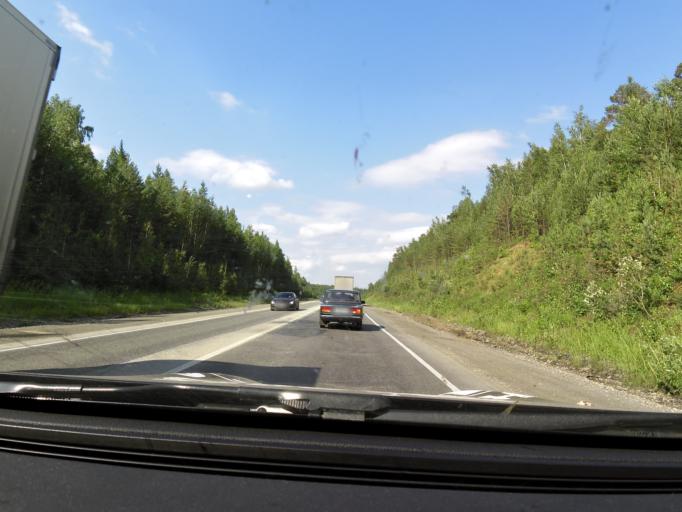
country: RU
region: Sverdlovsk
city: Talitsa
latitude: 56.8315
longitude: 59.9958
